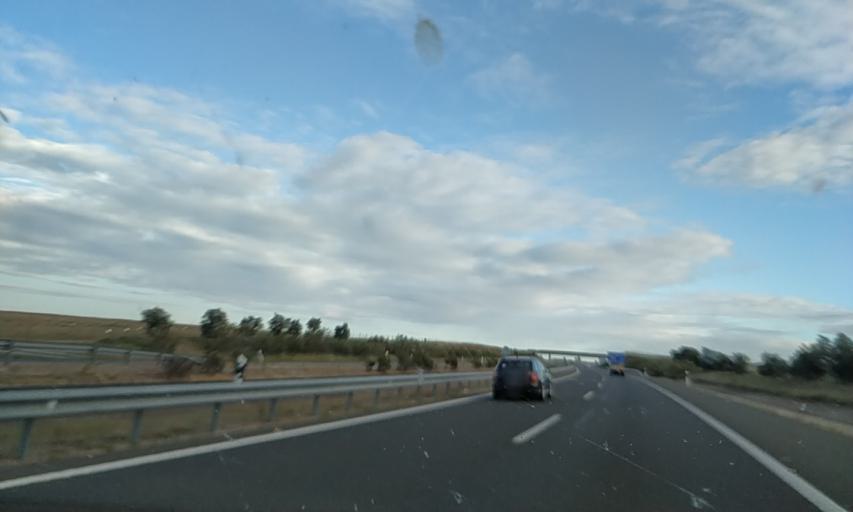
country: ES
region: Extremadura
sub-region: Provincia de Caceres
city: Casar de Caceres
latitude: 39.5666
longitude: -6.4013
